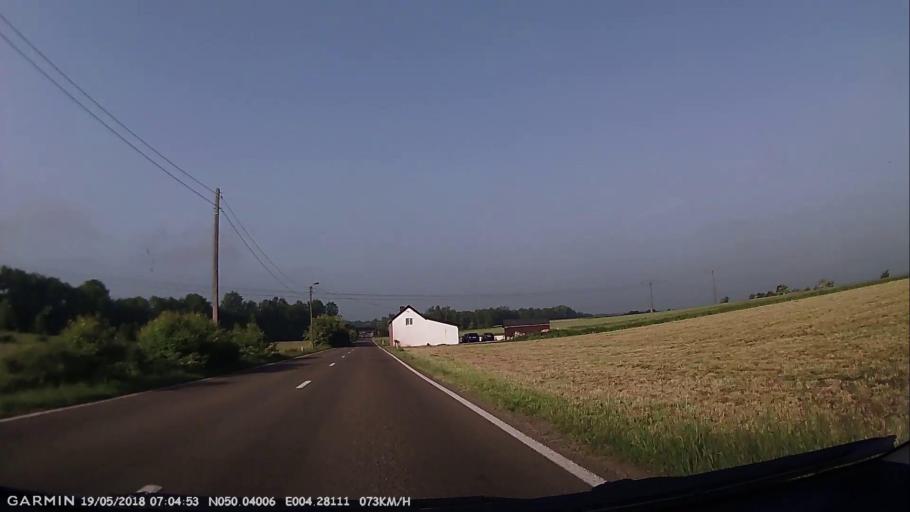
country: BE
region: Wallonia
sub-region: Province du Hainaut
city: Chimay
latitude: 50.0400
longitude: 4.2810
